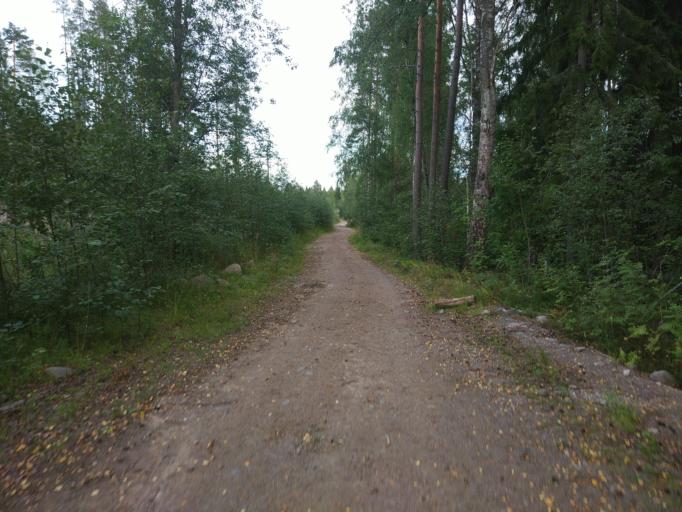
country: RU
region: Leningrad
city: Kuznechnoye
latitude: 61.1189
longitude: 29.5985
